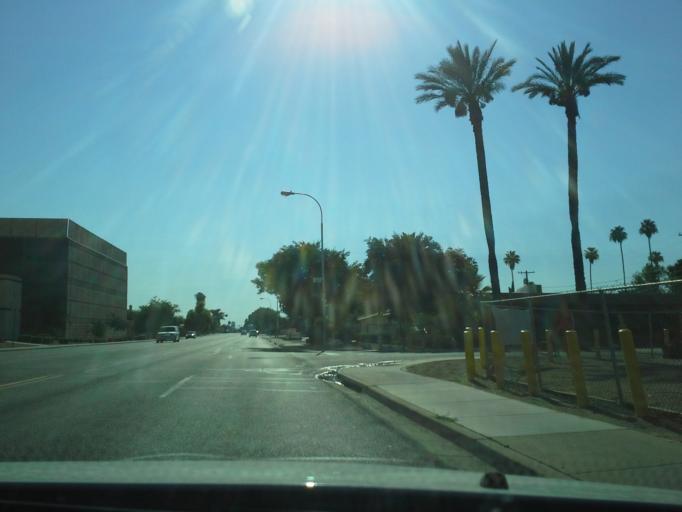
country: US
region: Arizona
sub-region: Maricopa County
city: Paradise Valley
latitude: 33.4953
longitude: -112.0065
